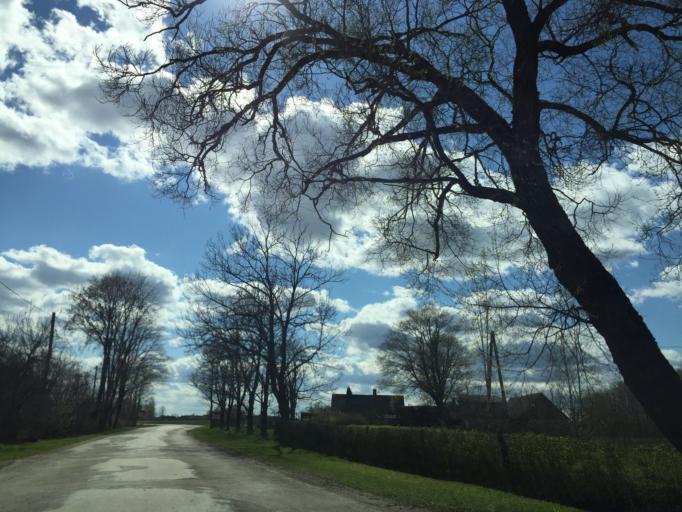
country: LV
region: Varaklani
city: Varaklani
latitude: 56.6009
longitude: 26.7335
